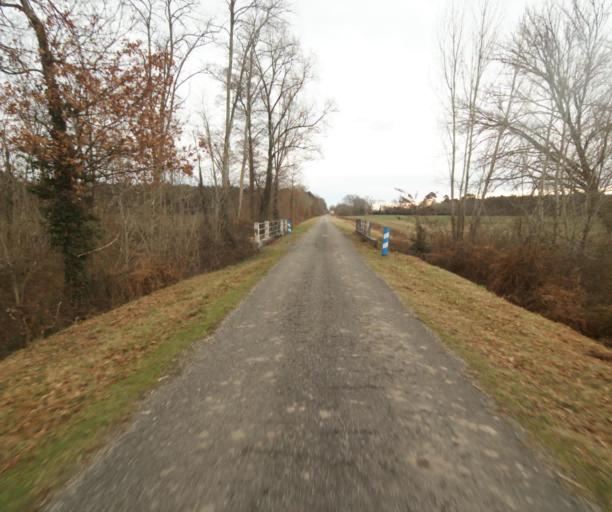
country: FR
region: Aquitaine
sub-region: Departement des Landes
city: Gabarret
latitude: 44.0185
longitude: -0.0409
